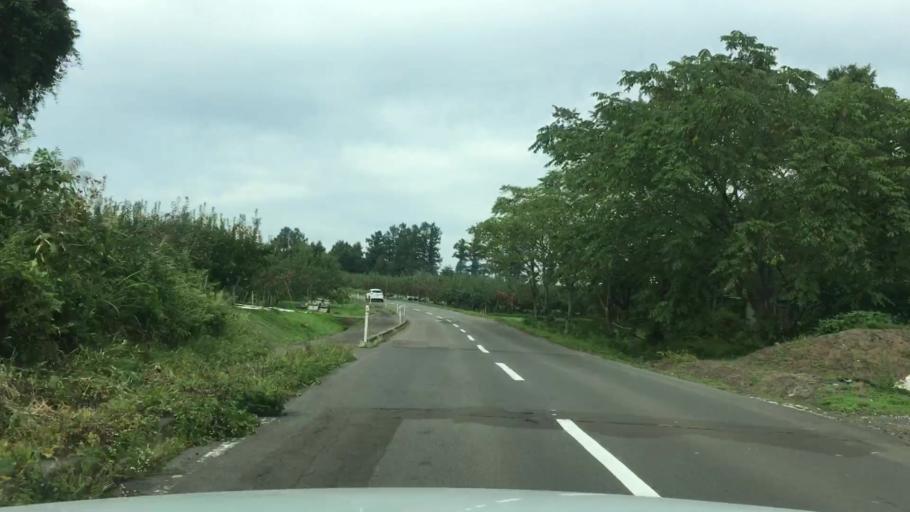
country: JP
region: Aomori
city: Hirosaki
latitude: 40.6762
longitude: 140.3812
